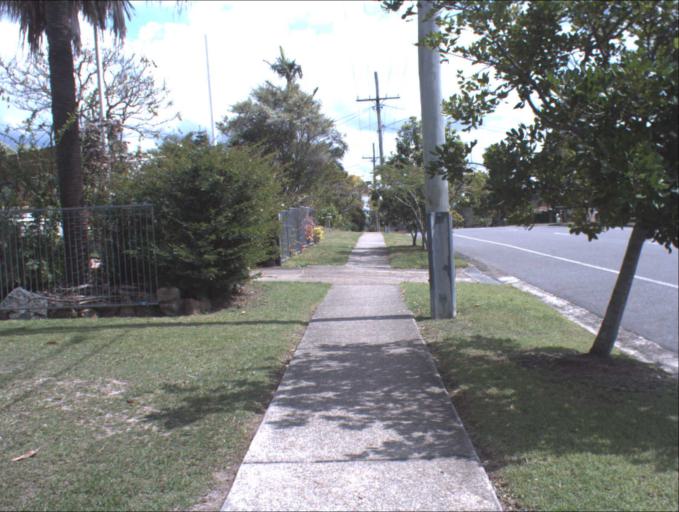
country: AU
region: Queensland
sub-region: Brisbane
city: Sunnybank Hills
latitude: -27.6561
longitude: 153.0494
